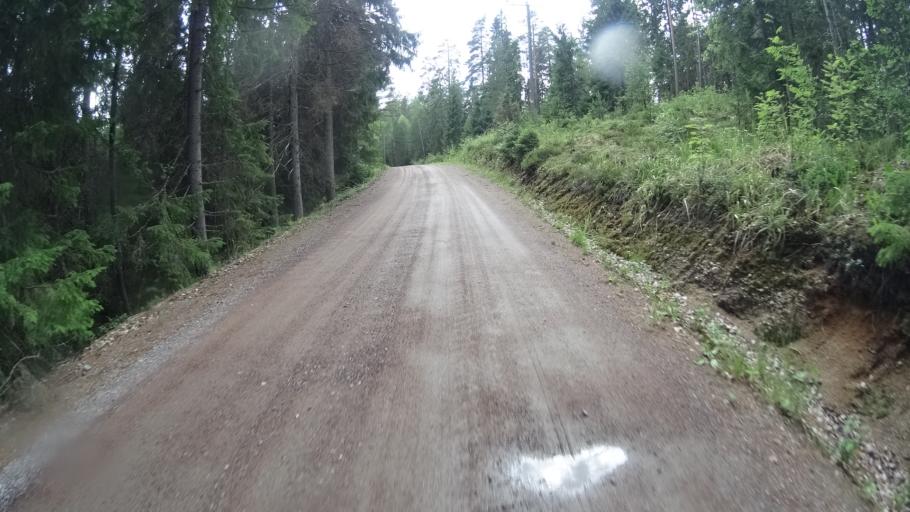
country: FI
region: Uusimaa
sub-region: Helsinki
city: Karkkila
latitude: 60.6060
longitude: 24.1847
